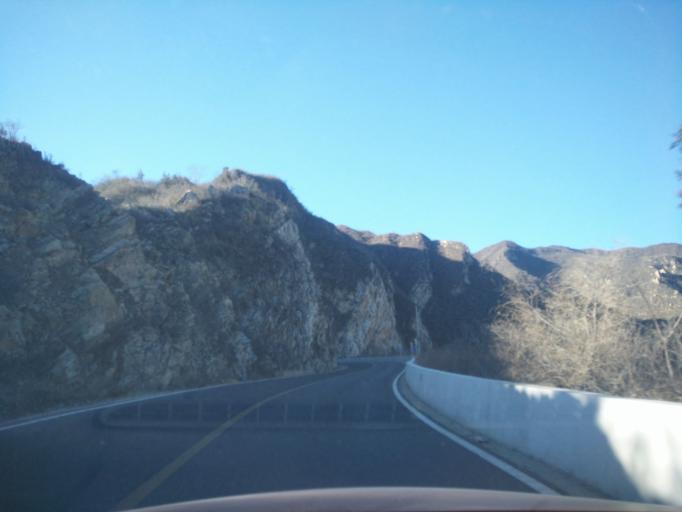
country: CN
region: Beijing
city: Wangping
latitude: 40.0072
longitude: 115.9781
